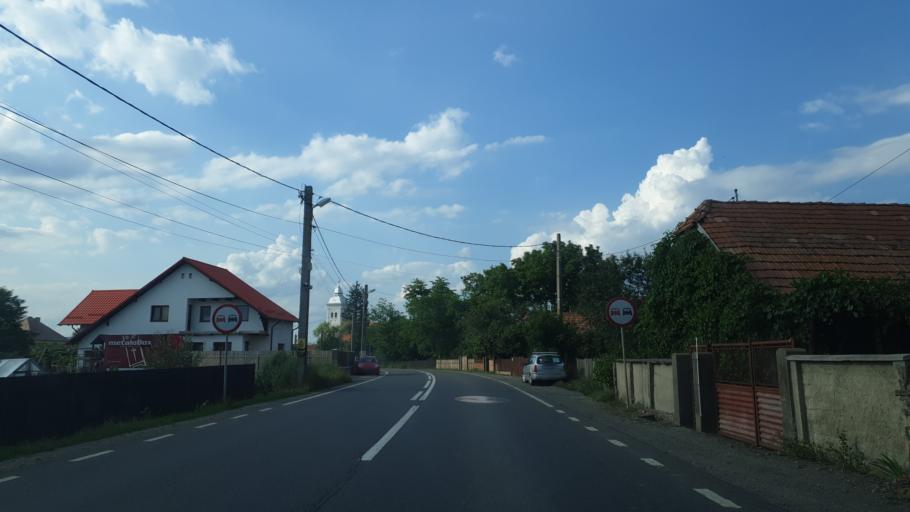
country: RO
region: Covasna
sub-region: Comuna Chichis
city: Chichis
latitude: 45.8110
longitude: 25.8003
